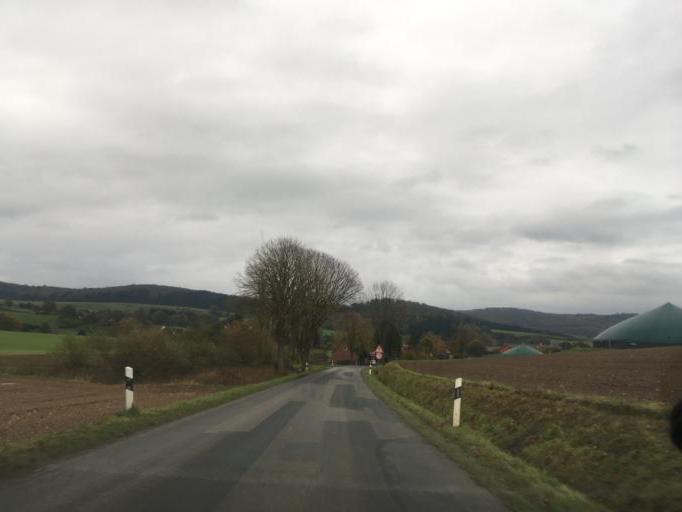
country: DE
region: Lower Saxony
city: Uslar
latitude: 51.6671
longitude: 9.6700
